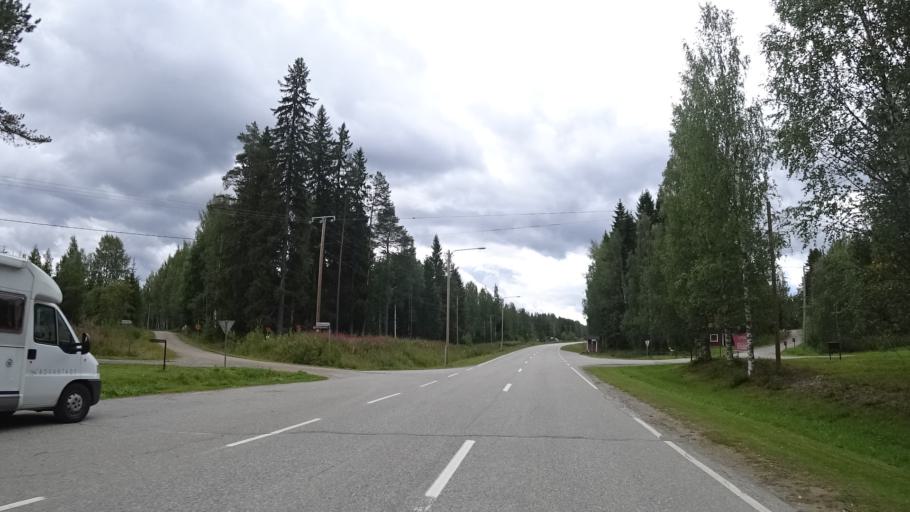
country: FI
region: North Karelia
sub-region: Joensuu
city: Ilomantsi
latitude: 62.6398
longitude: 31.2862
